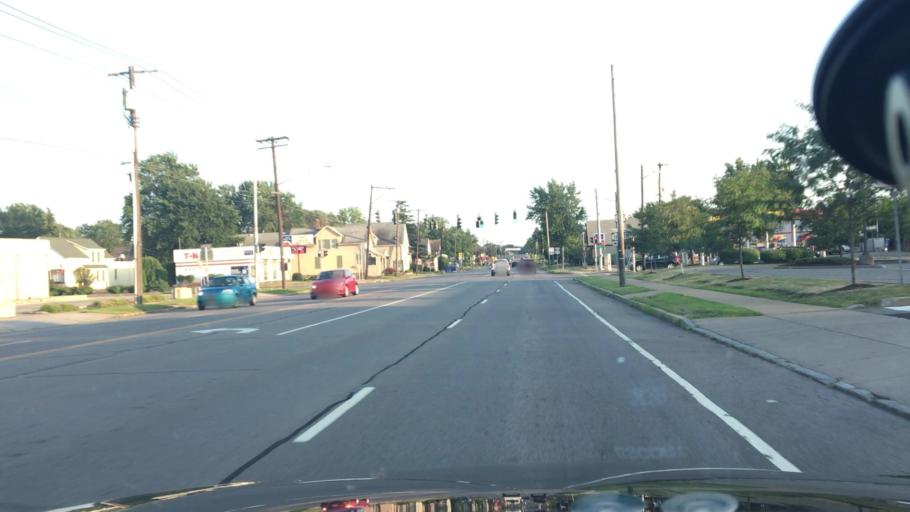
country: US
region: New York
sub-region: Erie County
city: West Seneca
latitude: 42.8402
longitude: -78.7543
